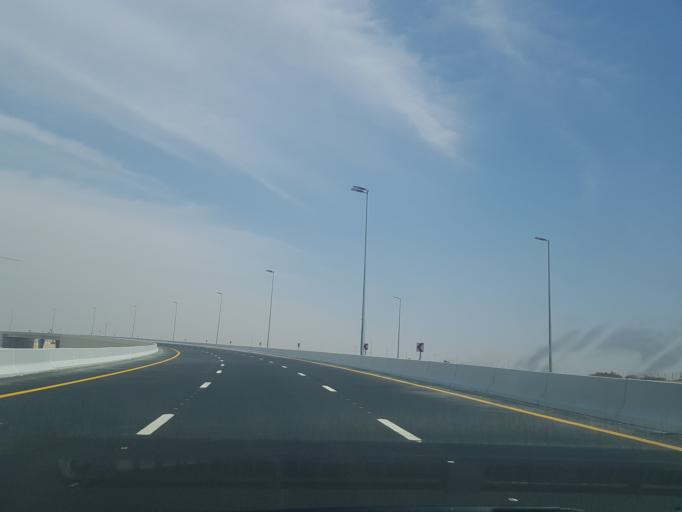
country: AE
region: Ash Shariqah
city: Sharjah
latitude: 25.2350
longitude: 55.5671
